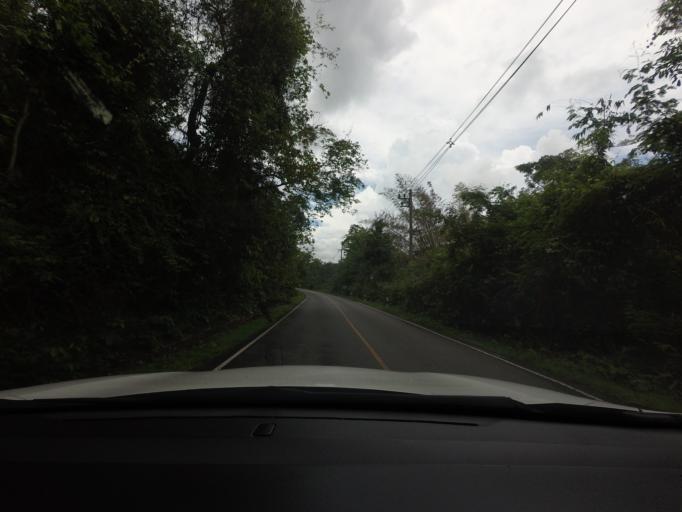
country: TH
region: Nakhon Ratchasima
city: Pak Chong
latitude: 14.4997
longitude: 101.3841
